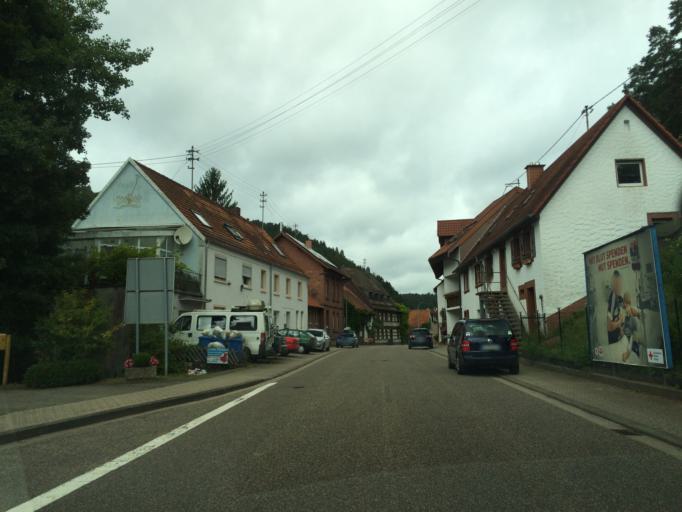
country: DE
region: Rheinland-Pfalz
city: Ruppertsweiler
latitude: 49.1696
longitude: 7.7197
